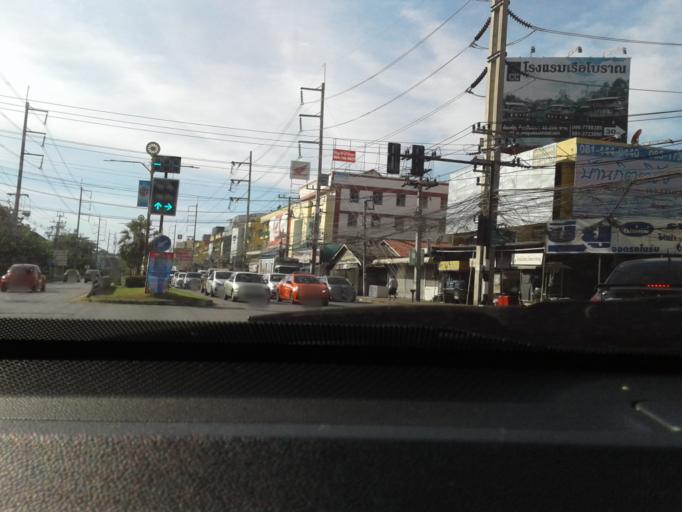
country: TH
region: Nakhon Pathom
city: Salaya
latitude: 13.8013
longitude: 100.3204
